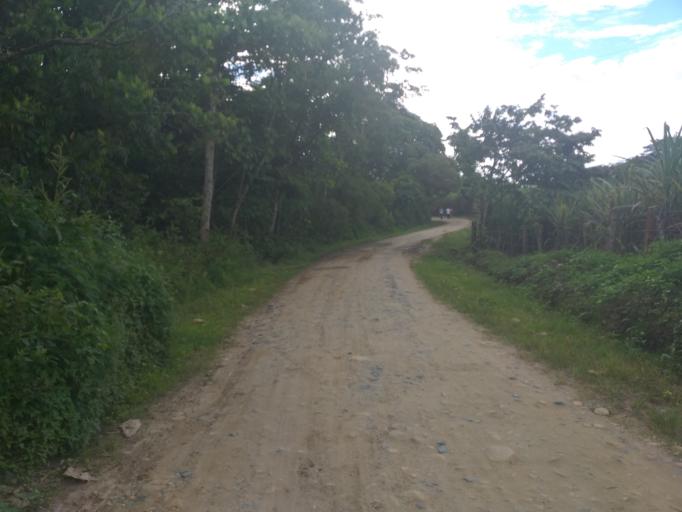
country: CO
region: Boyaca
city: Santana
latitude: 6.0518
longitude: -73.4939
